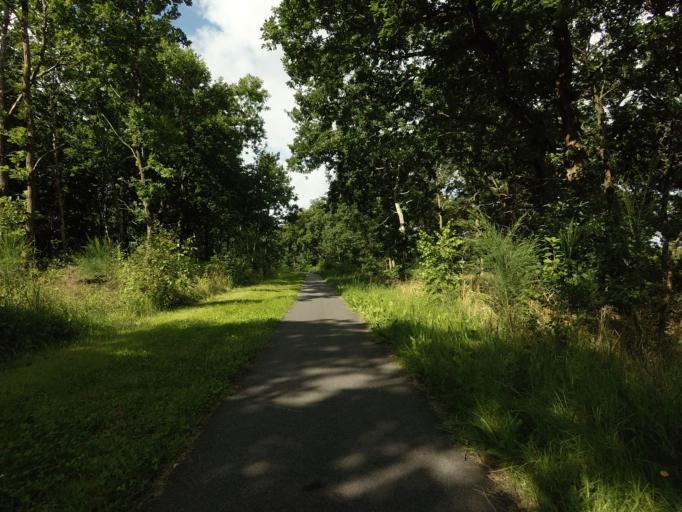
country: DK
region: Central Jutland
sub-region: Silkeborg Kommune
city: Svejbaek
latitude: 56.2113
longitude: 9.6771
